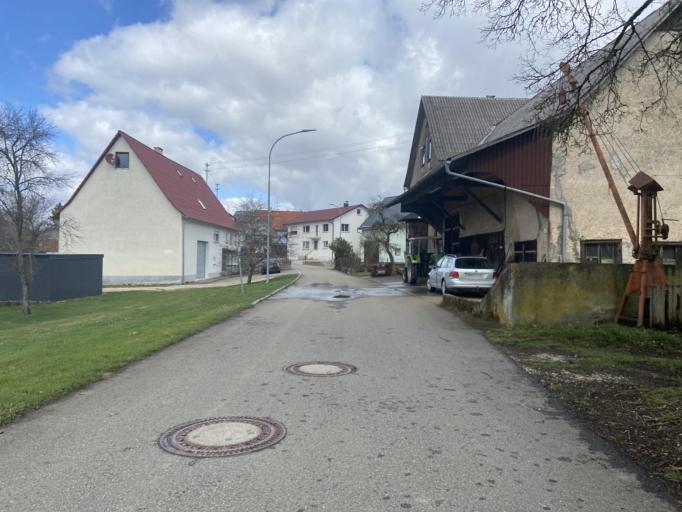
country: DE
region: Baden-Wuerttemberg
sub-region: Tuebingen Region
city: Veringenstadt
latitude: 48.1482
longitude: 9.2396
